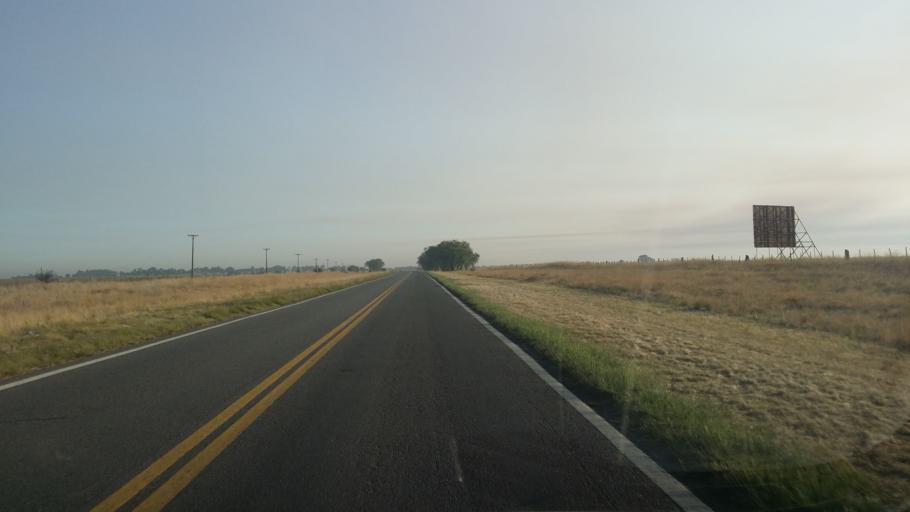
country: AR
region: La Pampa
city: Santa Rosa
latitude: -36.4955
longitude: -64.2799
